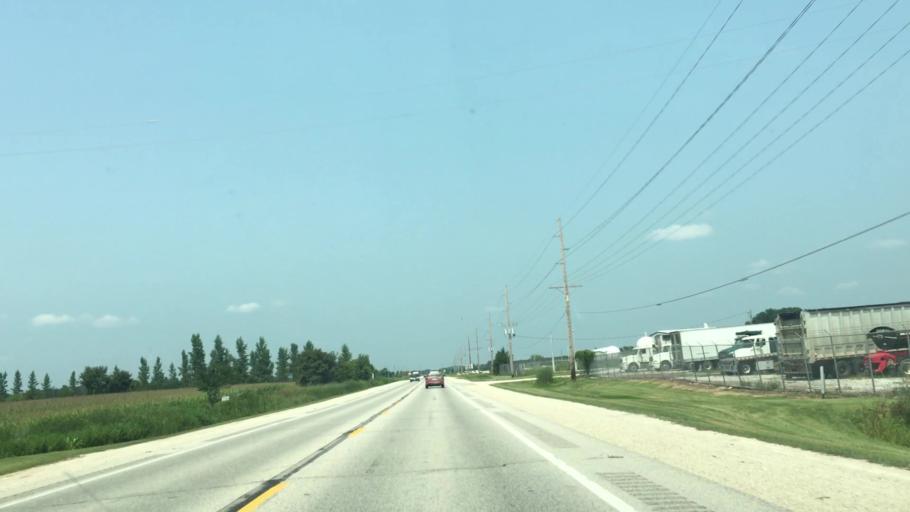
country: US
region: Iowa
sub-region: Fayette County
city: Oelwein
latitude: 42.6319
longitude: -91.9089
